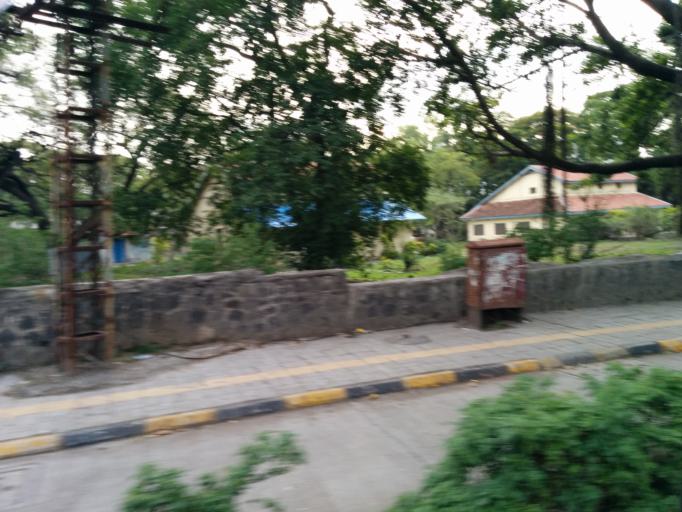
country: IN
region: Maharashtra
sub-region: Pune Division
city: Pune
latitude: 18.5042
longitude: 73.8784
